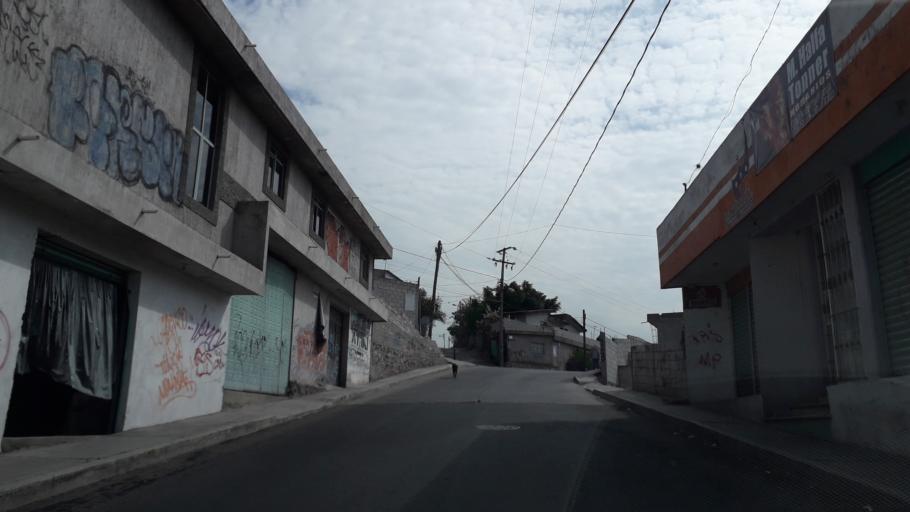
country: MX
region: Puebla
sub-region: Puebla
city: San Andres Azumiatla
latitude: 18.9048
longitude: -98.2504
